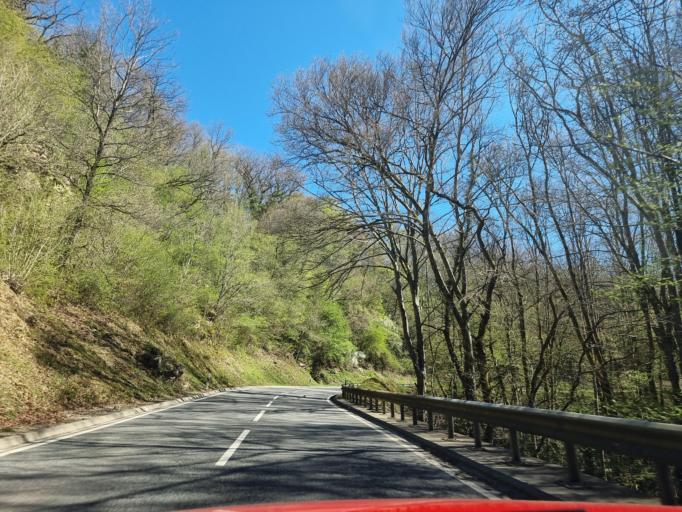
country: DE
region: Rheinland-Pfalz
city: Irrel
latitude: 49.8474
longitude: 6.4800
